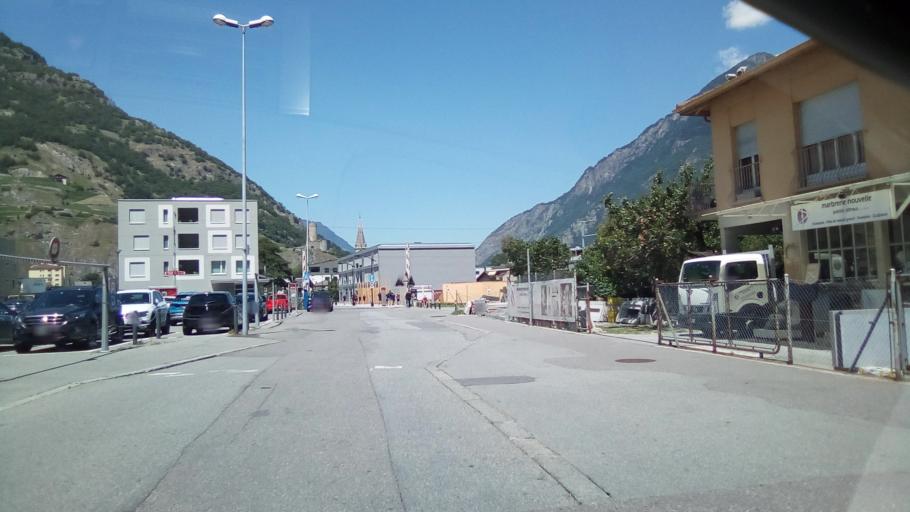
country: CH
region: Valais
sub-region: Martigny District
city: Martigny-Ville
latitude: 46.0972
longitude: 7.0767
